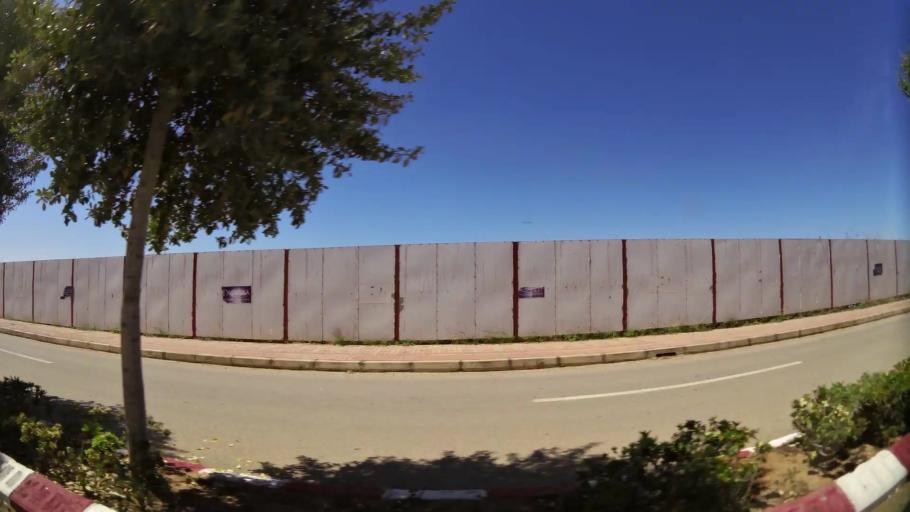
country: MA
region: Oriental
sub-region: Berkane-Taourirt
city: Madagh
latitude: 35.1087
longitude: -2.3125
